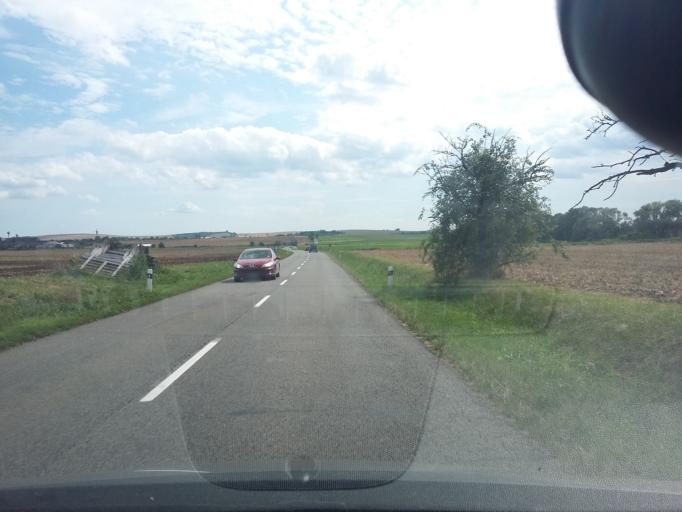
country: SK
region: Trnavsky
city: Gbely
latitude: 48.7413
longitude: 17.1696
